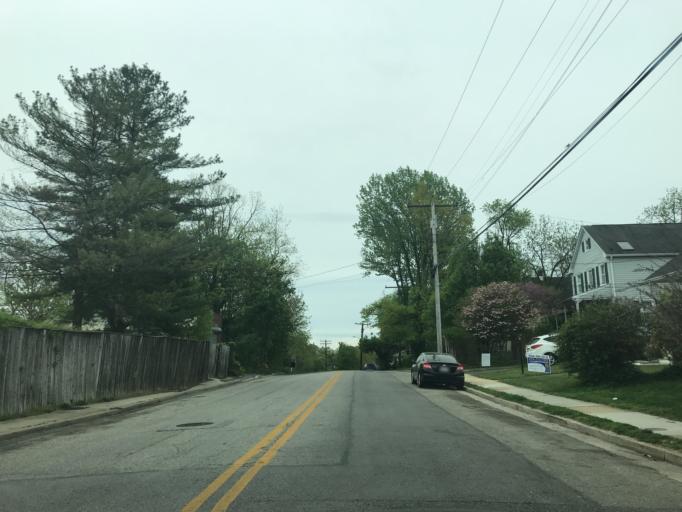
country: US
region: Maryland
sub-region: Baltimore County
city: Catonsville
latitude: 39.2678
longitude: -76.7326
